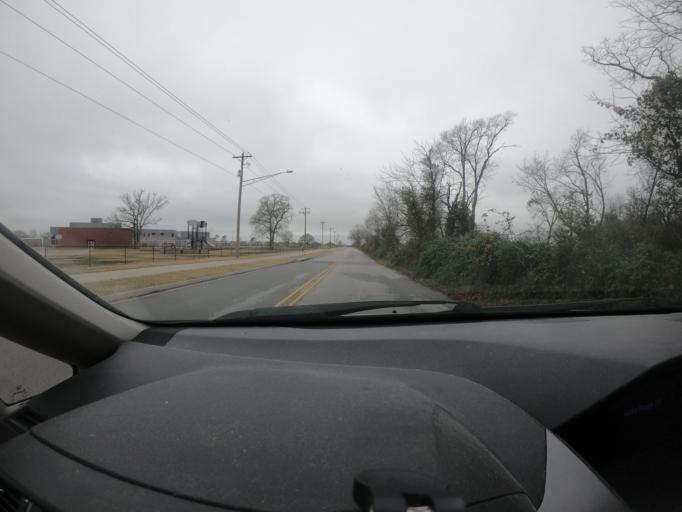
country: US
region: Arkansas
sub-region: Benton County
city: Bentonville
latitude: 36.3433
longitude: -94.2405
